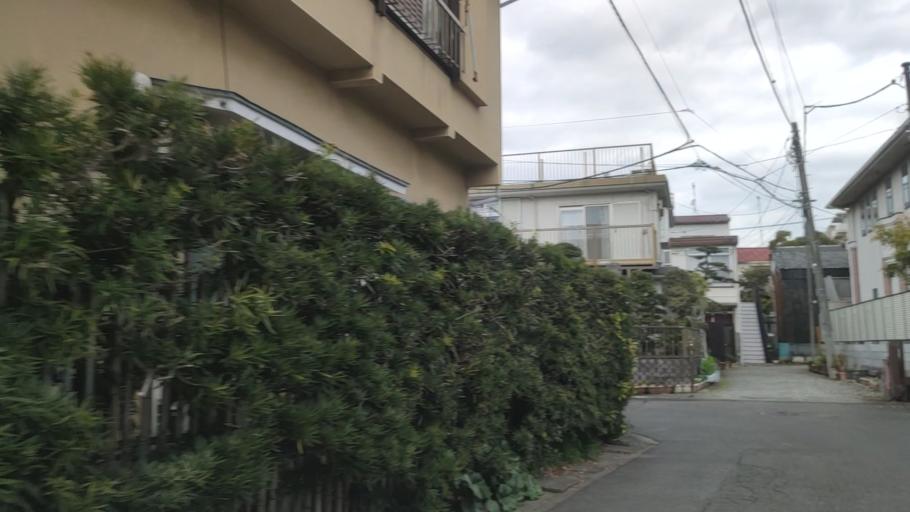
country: JP
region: Kanagawa
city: Odawara
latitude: 35.2458
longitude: 139.1563
